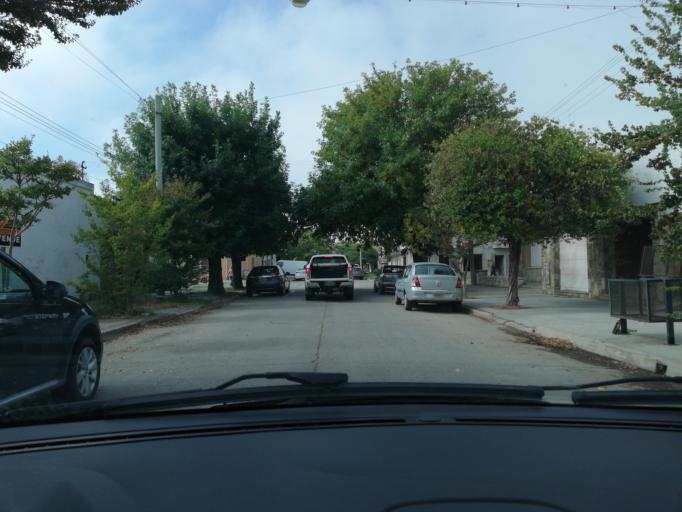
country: AR
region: Buenos Aires
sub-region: Partido de Balcarce
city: Balcarce
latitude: -37.8530
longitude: -58.2492
